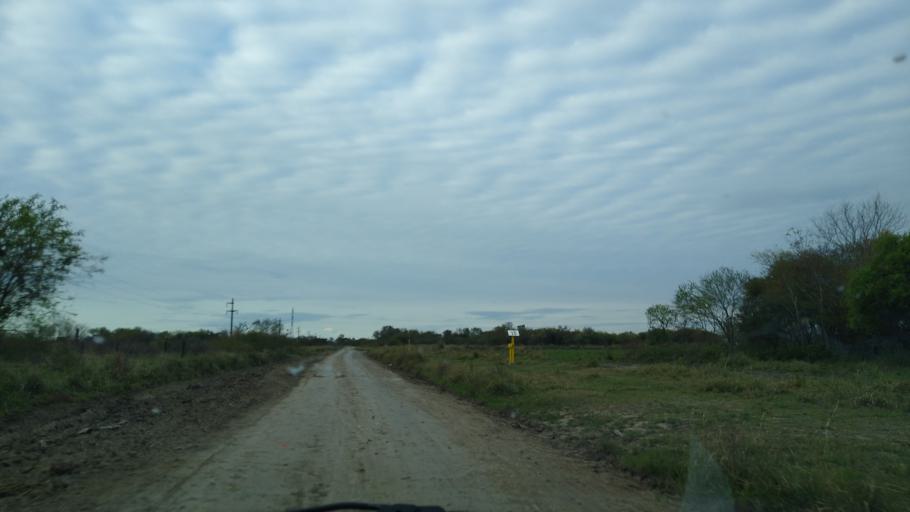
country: AR
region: Chaco
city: Puerto Tirol
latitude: -27.3894
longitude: -59.0485
